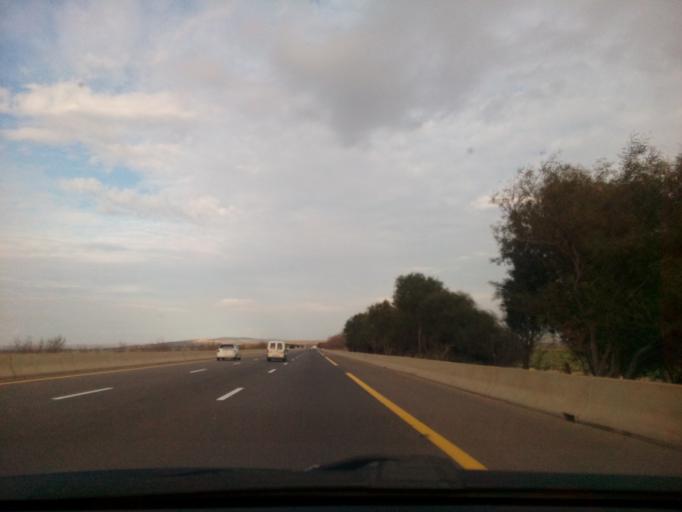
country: DZ
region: Mostaganem
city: Mostaganem
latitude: 35.6764
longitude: 0.1500
